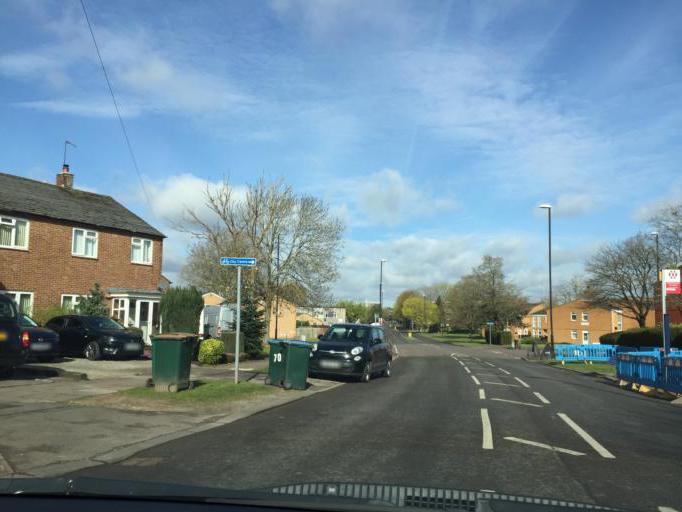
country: GB
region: England
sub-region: Coventry
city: Coventry
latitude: 52.3880
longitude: -1.4977
